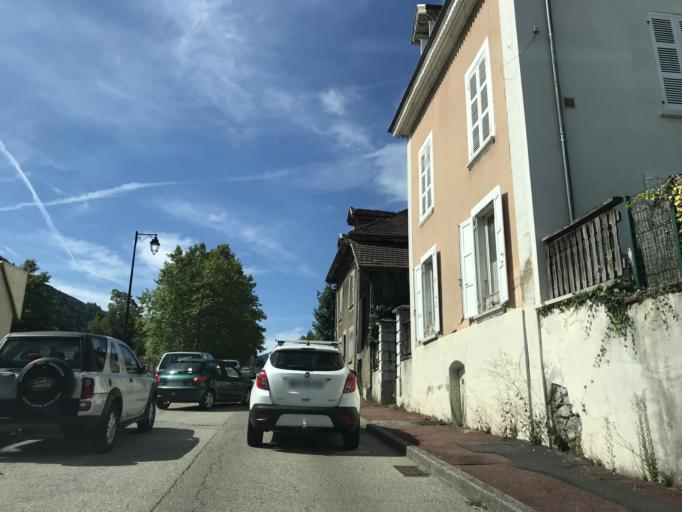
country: FR
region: Rhone-Alpes
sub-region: Departement de l'Isere
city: Allevard
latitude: 45.3916
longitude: 6.0720
